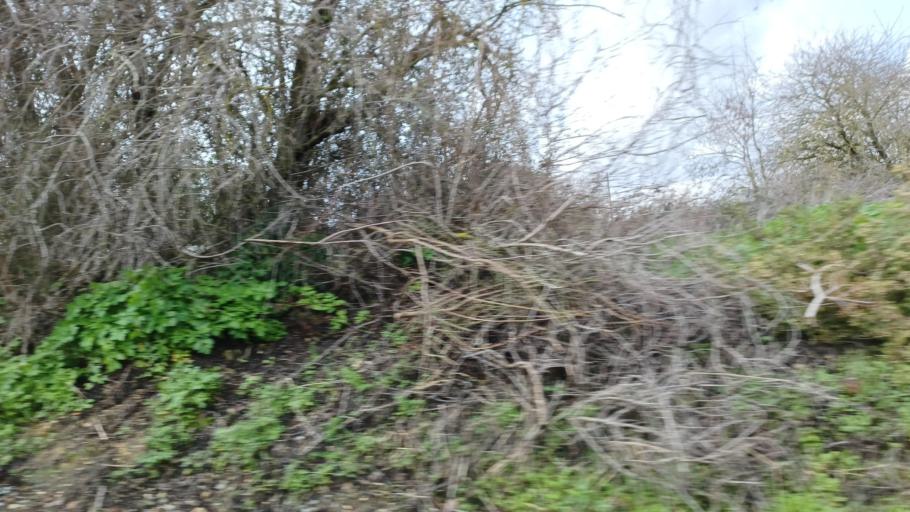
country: CY
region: Pafos
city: Mesogi
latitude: 34.8830
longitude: 32.5058
